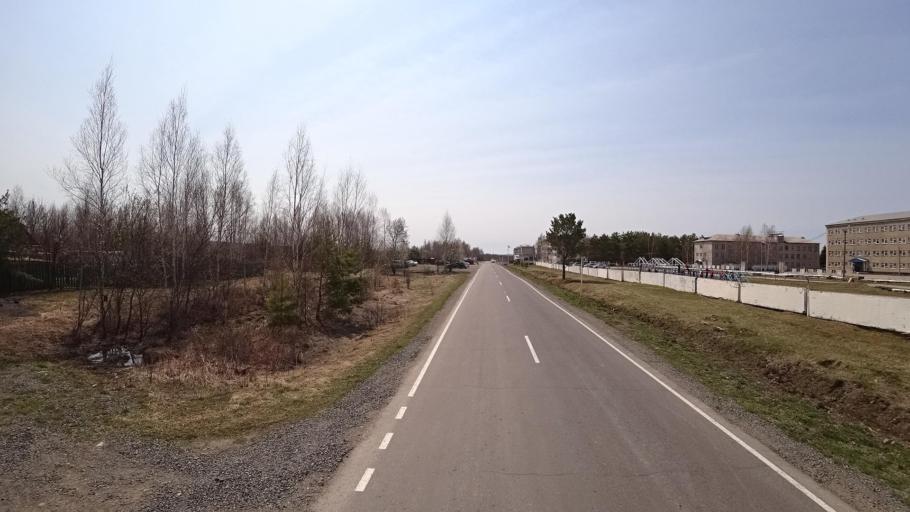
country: RU
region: Khabarovsk Krai
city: Selikhino
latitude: 50.3915
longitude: 137.3741
